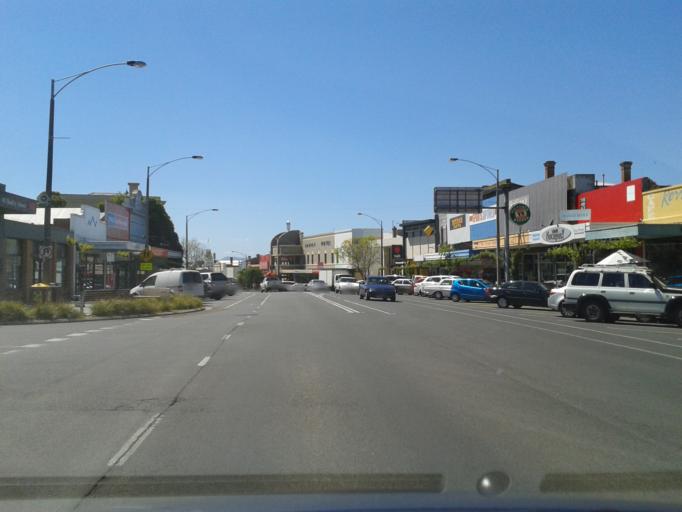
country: AU
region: Victoria
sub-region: Ararat
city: Ararat
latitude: -37.2843
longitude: 142.9282
